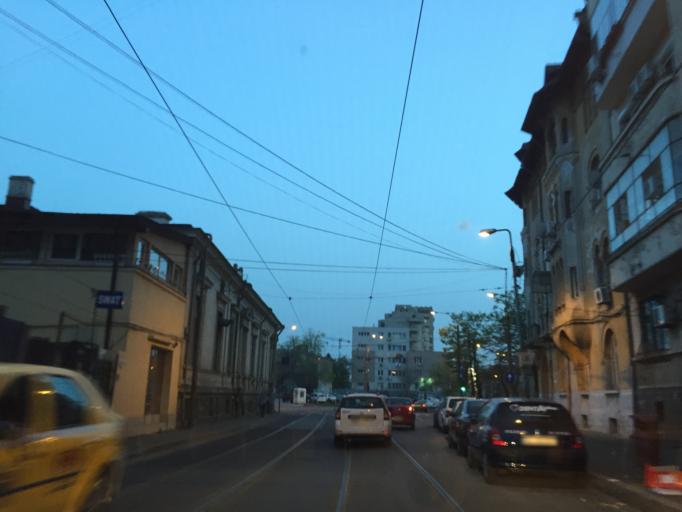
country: RO
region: Bucuresti
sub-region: Municipiul Bucuresti
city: Bucharest
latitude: 44.4334
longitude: 26.1120
